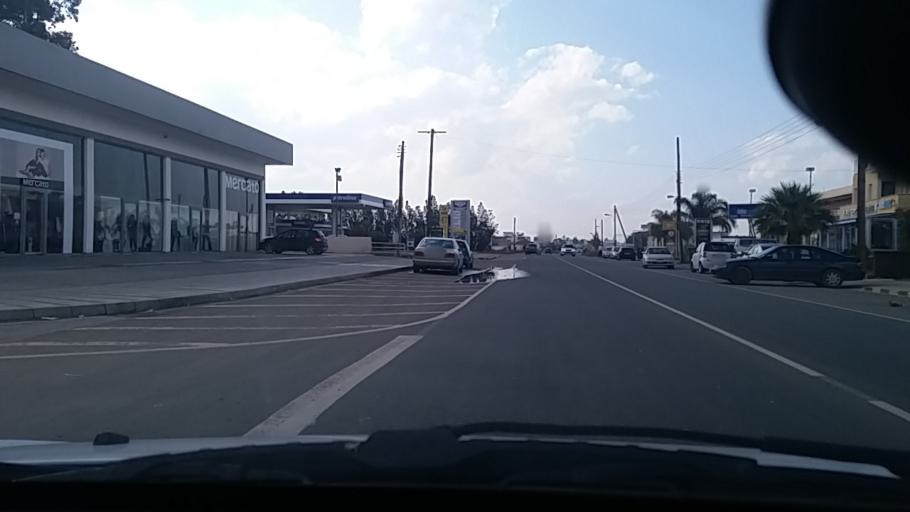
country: CY
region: Lefkosia
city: Kokkinotrimithia
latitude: 35.1490
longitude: 33.2131
